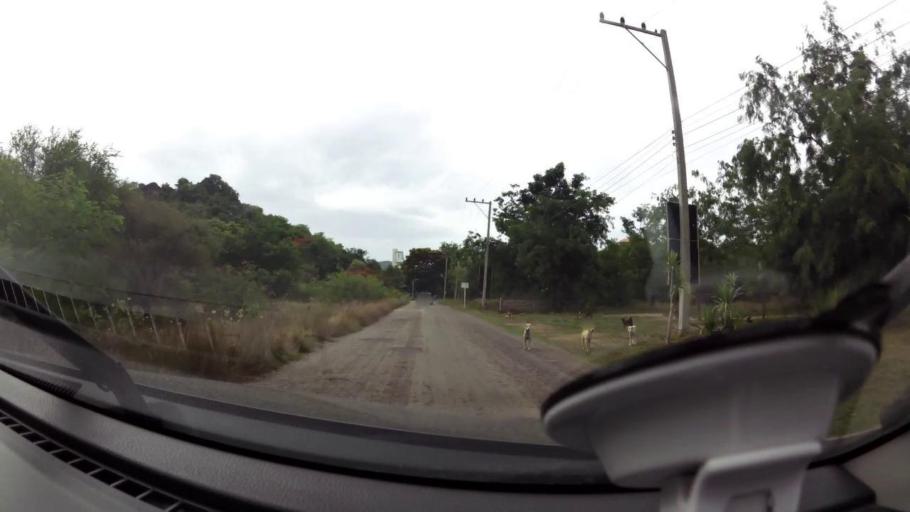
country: TH
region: Prachuap Khiri Khan
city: Pran Buri
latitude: 12.4243
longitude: 99.9794
